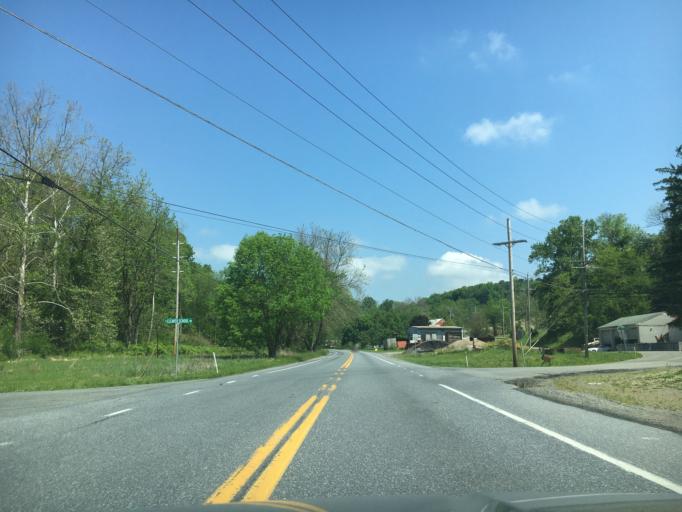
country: US
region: Pennsylvania
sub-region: Berks County
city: New Berlinville
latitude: 40.3507
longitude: -75.6623
